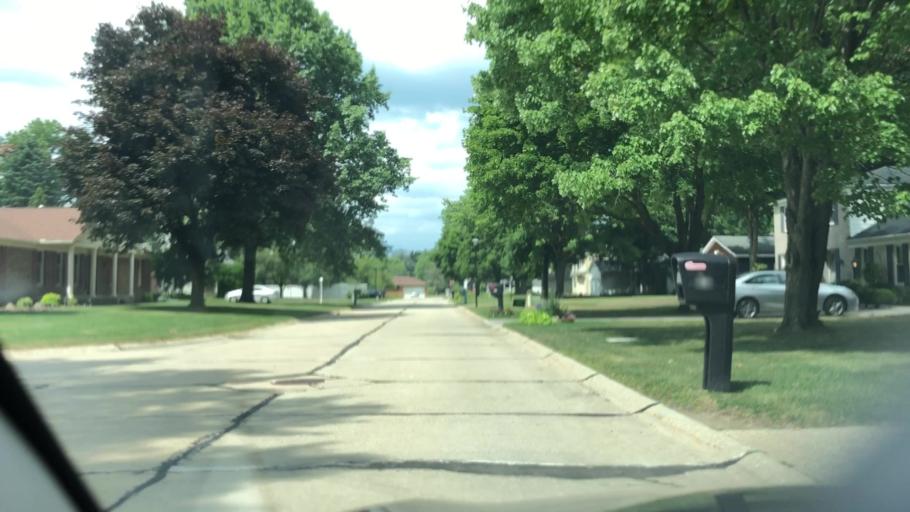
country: US
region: Ohio
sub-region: Summit County
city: Fairlawn
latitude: 41.1245
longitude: -81.6333
